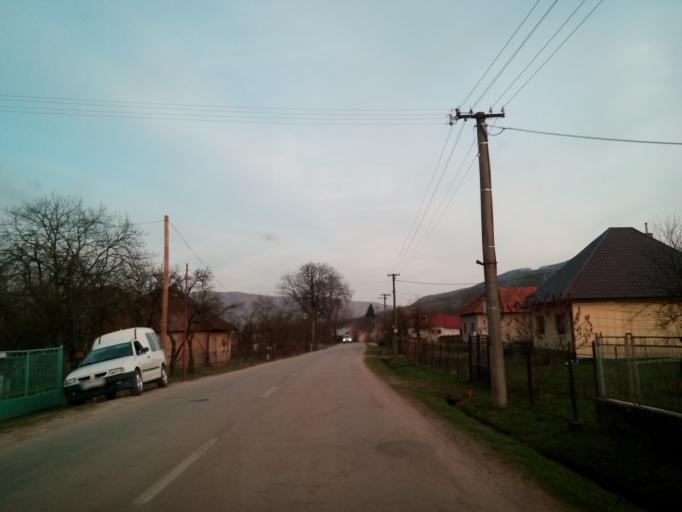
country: SK
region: Kosicky
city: Dobsina
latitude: 48.6863
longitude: 20.3251
